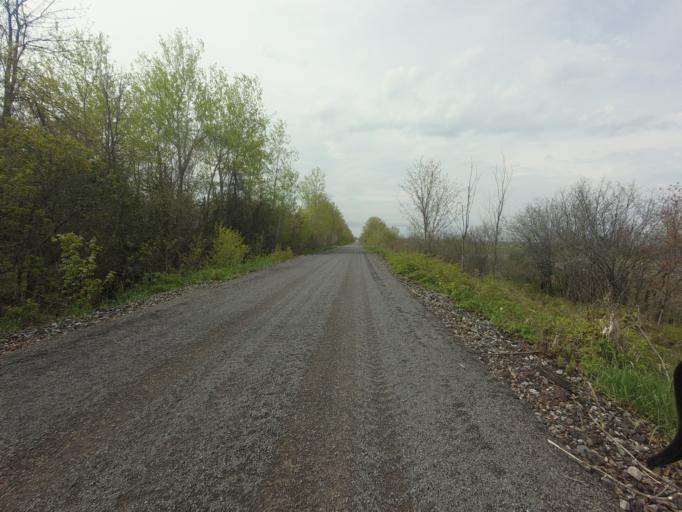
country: CA
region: Ontario
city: Carleton Place
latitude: 45.1658
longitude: -76.1485
